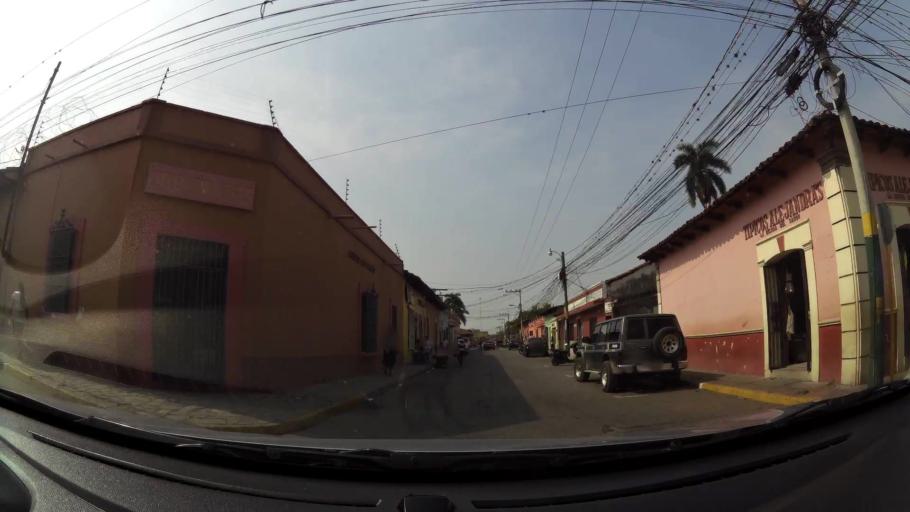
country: HN
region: Comayagua
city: Comayagua
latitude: 14.4582
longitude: -87.6400
